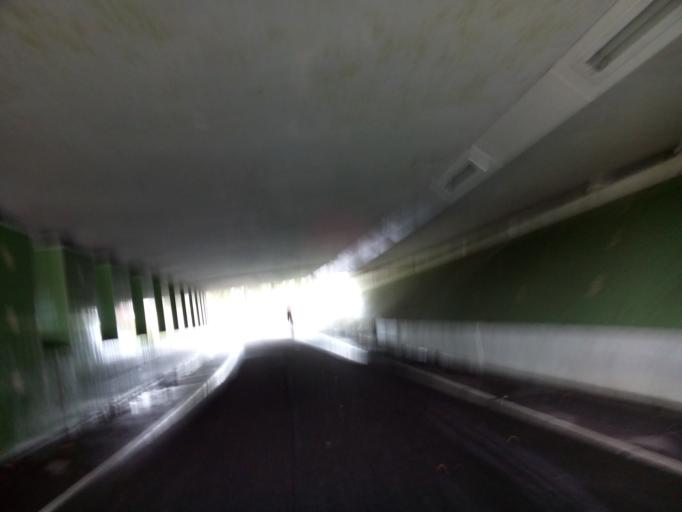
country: NL
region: Utrecht
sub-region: Gemeente Montfoort
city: Montfoort
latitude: 52.1007
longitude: 4.9396
